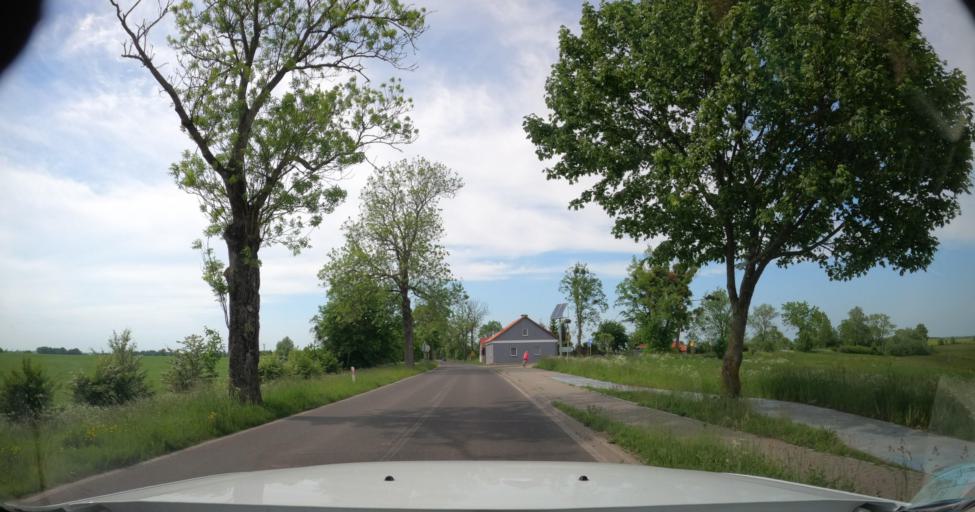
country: PL
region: Warmian-Masurian Voivodeship
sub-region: Powiat lidzbarski
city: Lidzbark Warminski
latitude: 54.1480
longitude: 20.5590
